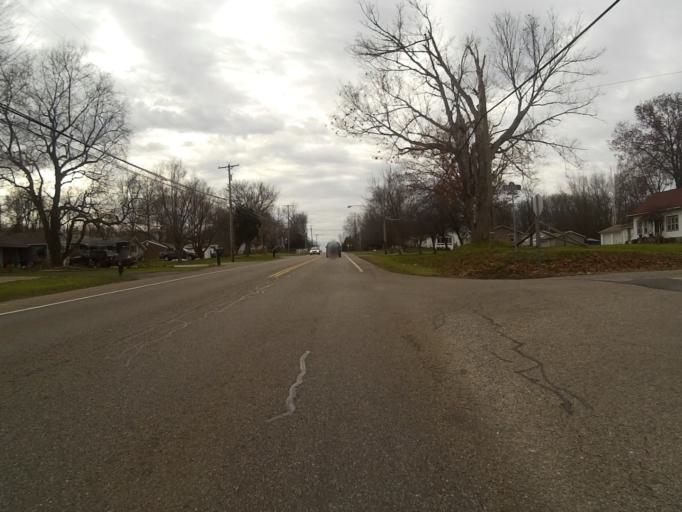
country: US
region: Ohio
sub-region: Portage County
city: Brimfield
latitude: 41.0911
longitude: -81.3466
